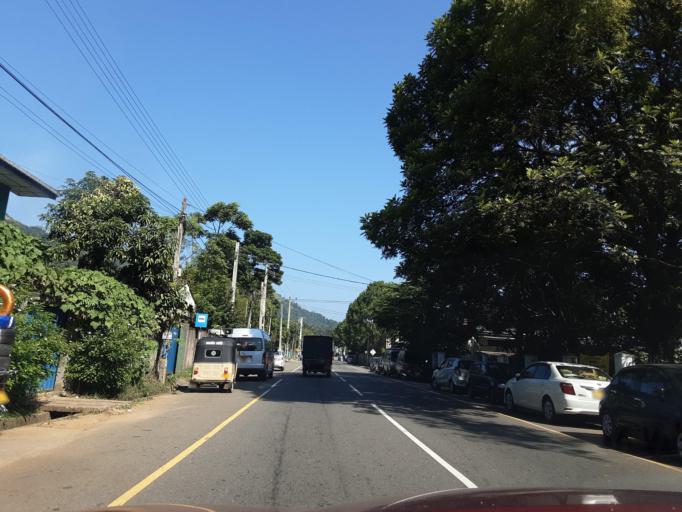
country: LK
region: Uva
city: Badulla
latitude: 6.9948
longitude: 81.0577
